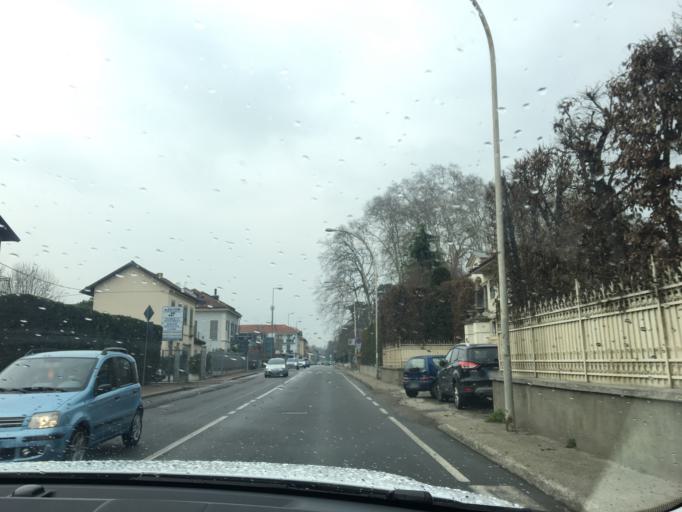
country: IT
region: Piedmont
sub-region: Provincia di Torino
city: Moncalieri
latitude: 45.0171
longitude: 7.6800
